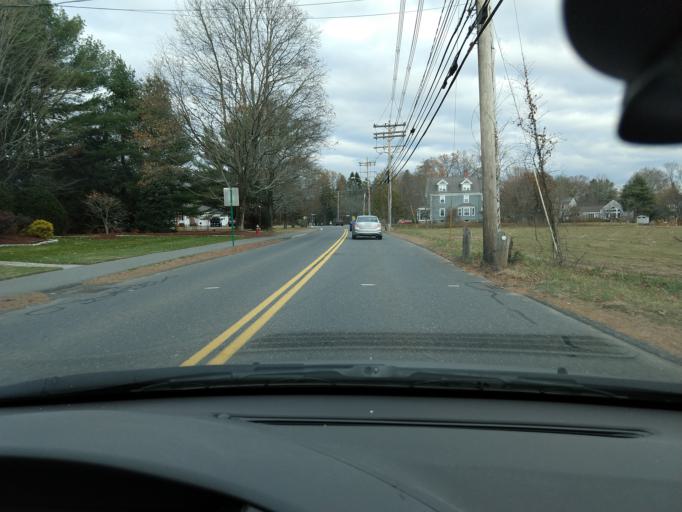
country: US
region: Massachusetts
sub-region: Middlesex County
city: Concord
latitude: 42.4647
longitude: -71.3221
